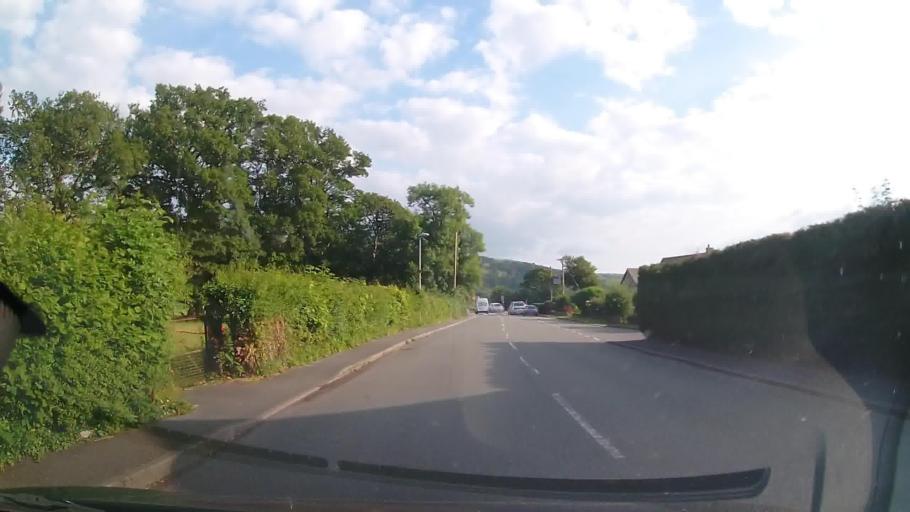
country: GB
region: Wales
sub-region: Gwynedd
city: Bala
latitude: 52.9065
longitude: -3.5946
